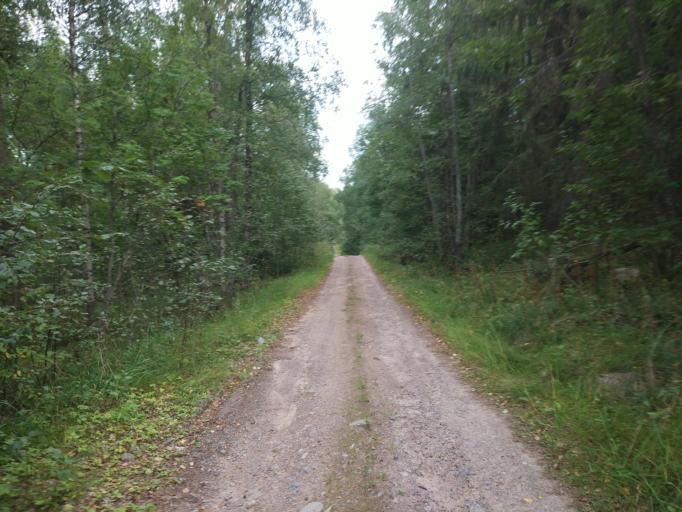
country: RU
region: Leningrad
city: Kuznechnoye
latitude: 61.1124
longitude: 29.6102
